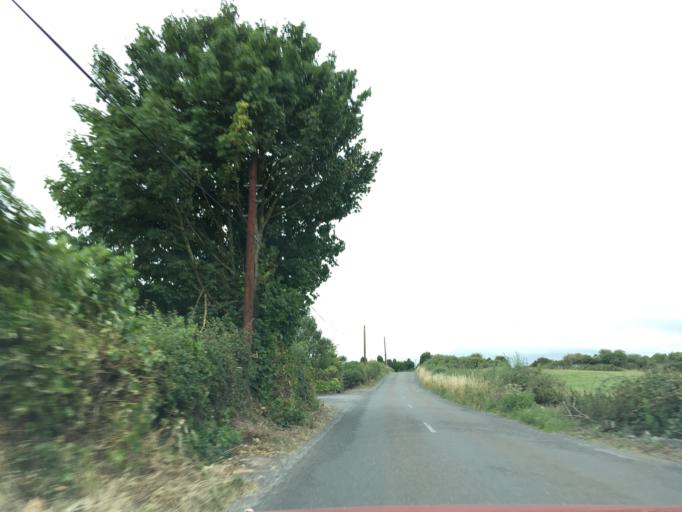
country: IE
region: Munster
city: Cashel
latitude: 52.4765
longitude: -7.8905
